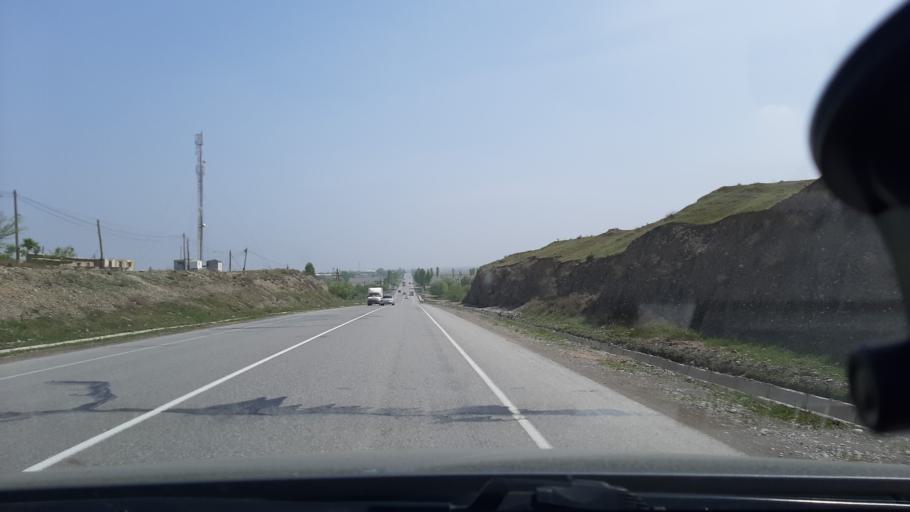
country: UZ
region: Toshkent
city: Bekobod
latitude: 40.1255
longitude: 69.2396
